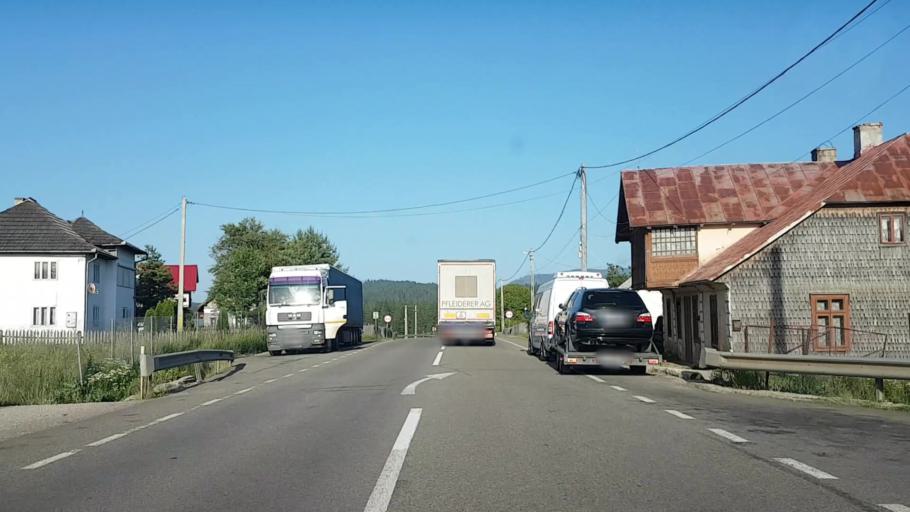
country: RO
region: Suceava
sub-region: Comuna Poiana Stampei
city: Poiana Stampei
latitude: 47.3001
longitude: 25.1040
